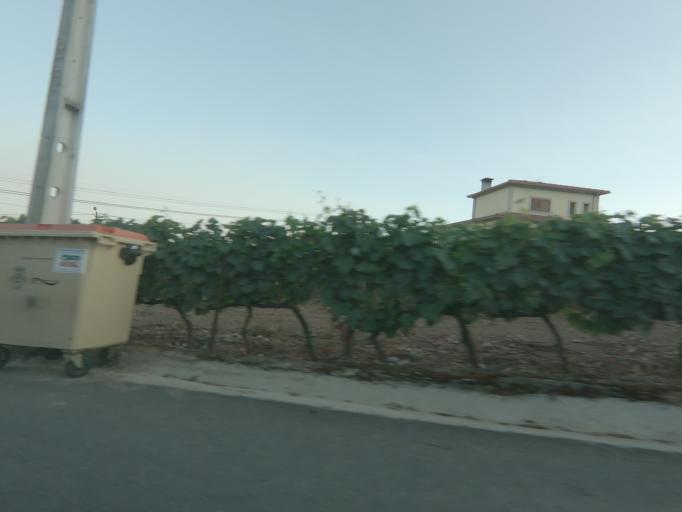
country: PT
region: Vila Real
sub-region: Sabrosa
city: Vilela
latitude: 41.2095
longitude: -7.6710
